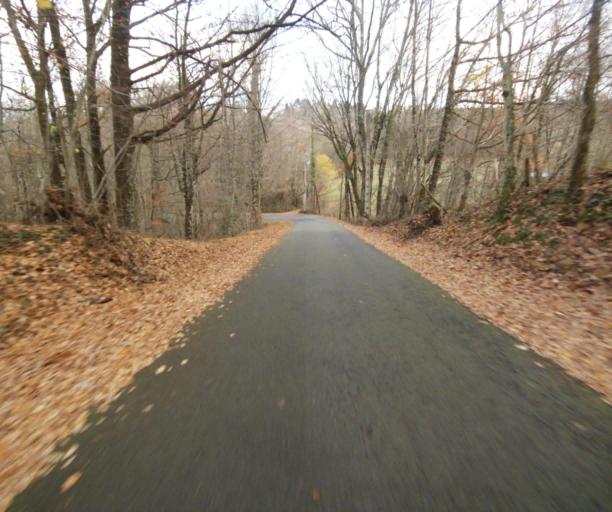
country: FR
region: Limousin
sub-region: Departement de la Correze
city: Sainte-Fortunade
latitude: 45.2101
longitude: 1.7824
